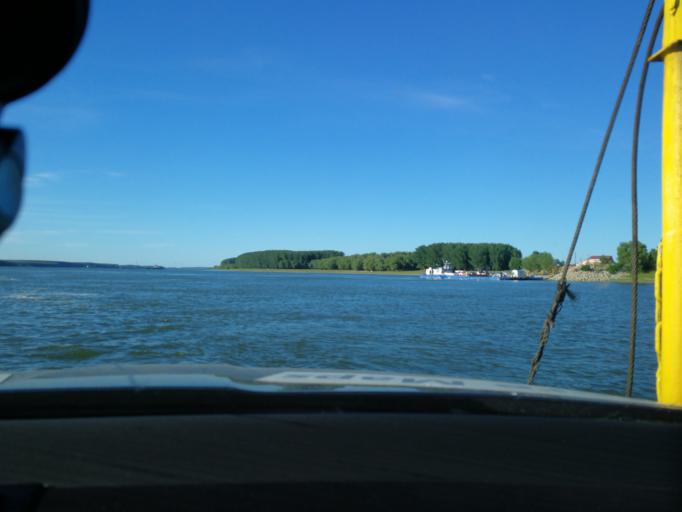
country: RO
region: Braila
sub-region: Municipiul Braila
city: Braila
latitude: 45.2868
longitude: 27.9950
